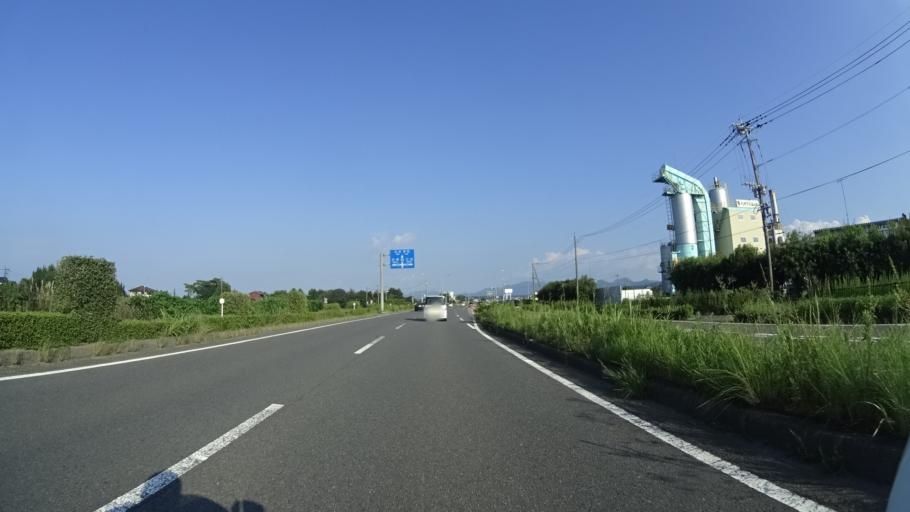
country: JP
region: Fukuoka
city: Nakatsu
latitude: 33.5532
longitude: 131.2605
